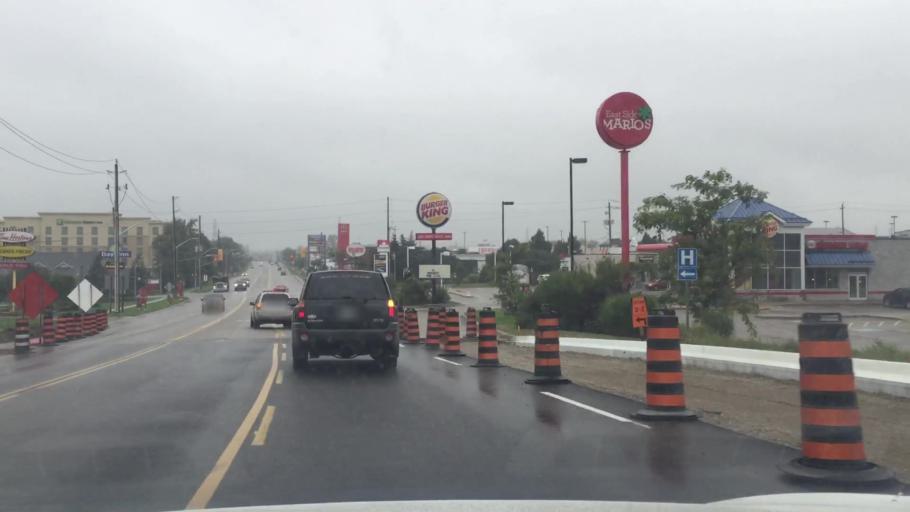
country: CA
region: Ontario
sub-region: Oxford County
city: Woodstock
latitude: 43.1123
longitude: -80.7366
